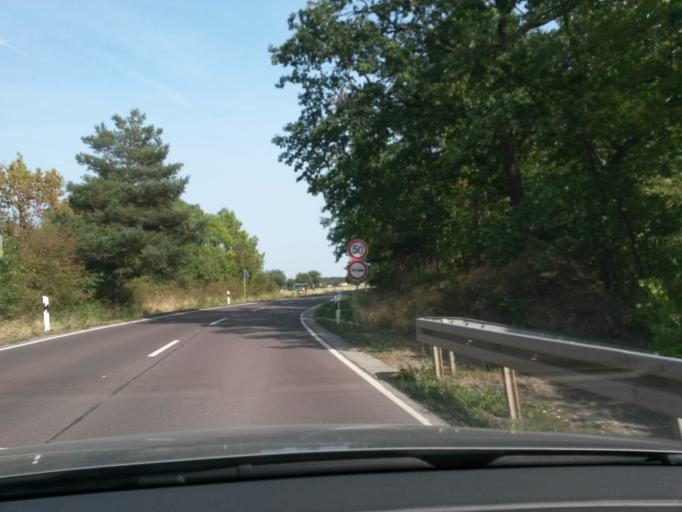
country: DE
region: Saxony-Anhalt
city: Rogatz
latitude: 52.2692
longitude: 11.7655
